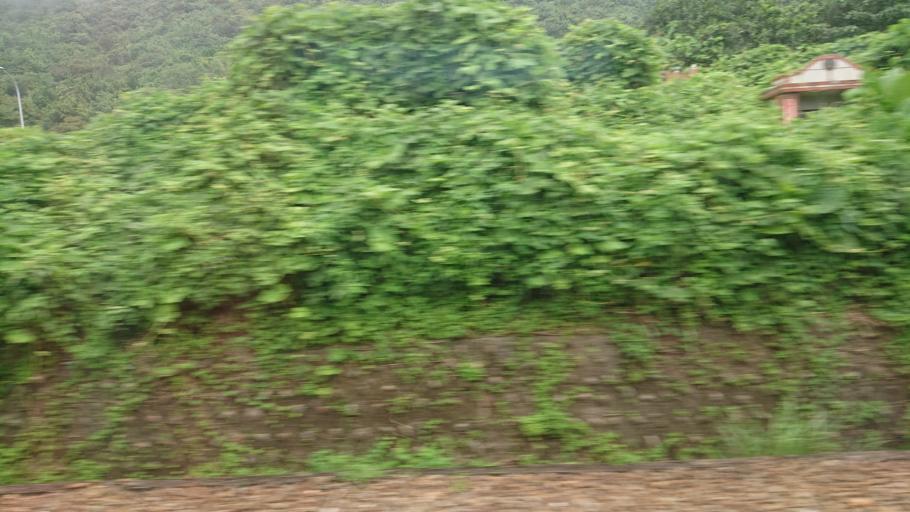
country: TW
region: Taiwan
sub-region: Keelung
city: Keelung
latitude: 24.9682
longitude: 121.9241
